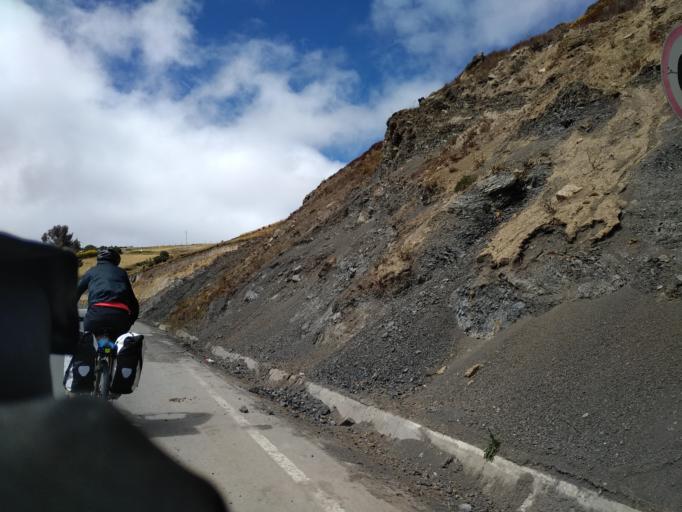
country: EC
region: Cotopaxi
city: Pujili
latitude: -0.9464
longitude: -78.9210
